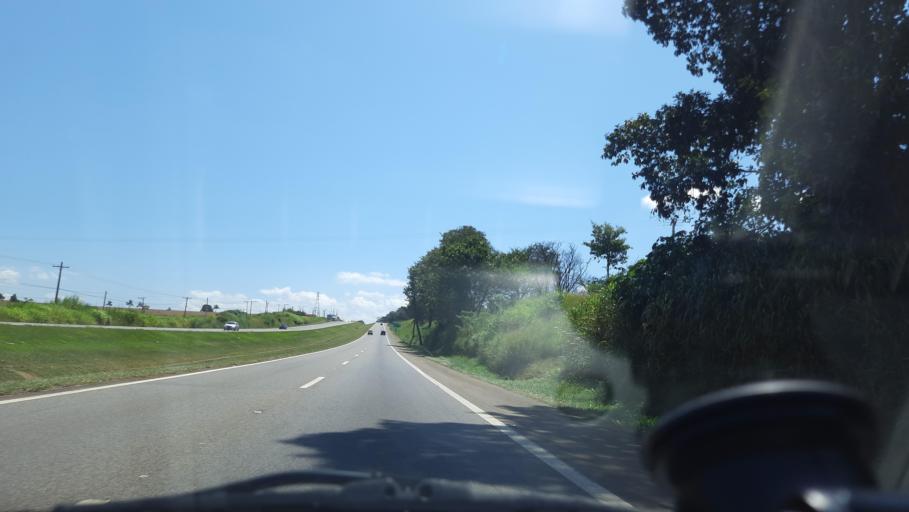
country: BR
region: Sao Paulo
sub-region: Mogi-Mirim
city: Mogi Mirim
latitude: -22.4985
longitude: -46.9837
